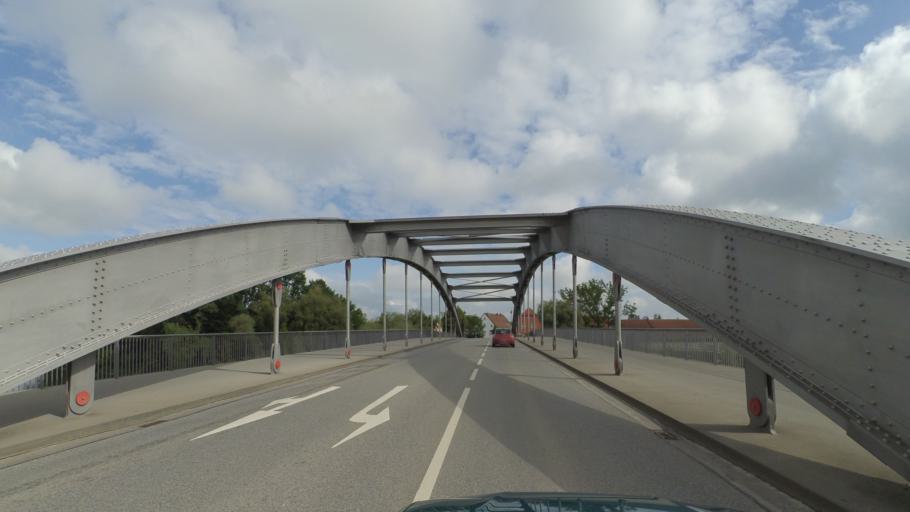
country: DE
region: Bavaria
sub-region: Lower Bavaria
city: Straubing
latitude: 48.8856
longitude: 12.5740
